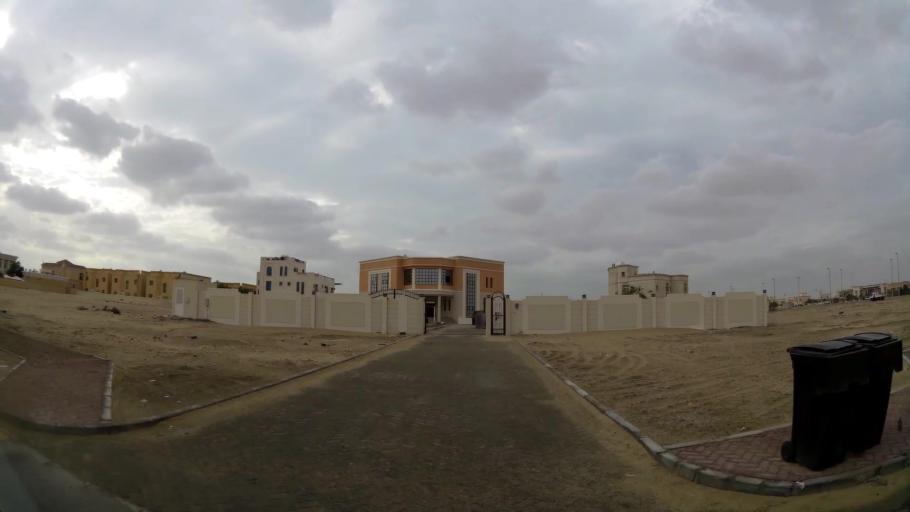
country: AE
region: Abu Dhabi
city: Abu Dhabi
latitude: 24.3491
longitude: 54.6217
